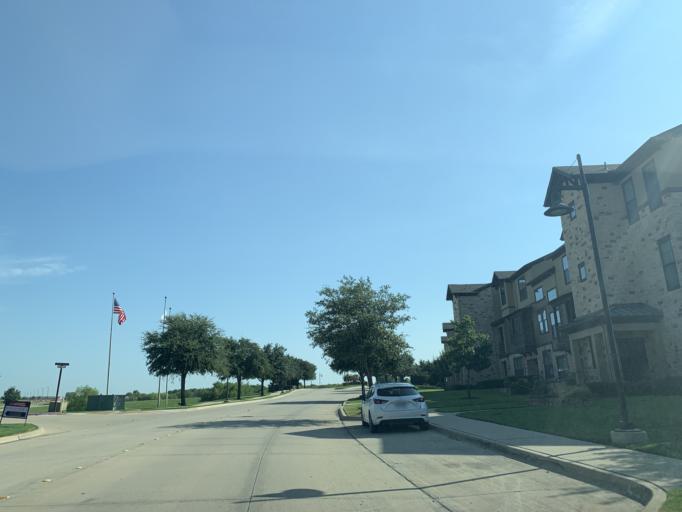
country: US
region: Texas
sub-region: Tarrant County
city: Blue Mound
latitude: 32.8949
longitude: -97.3120
